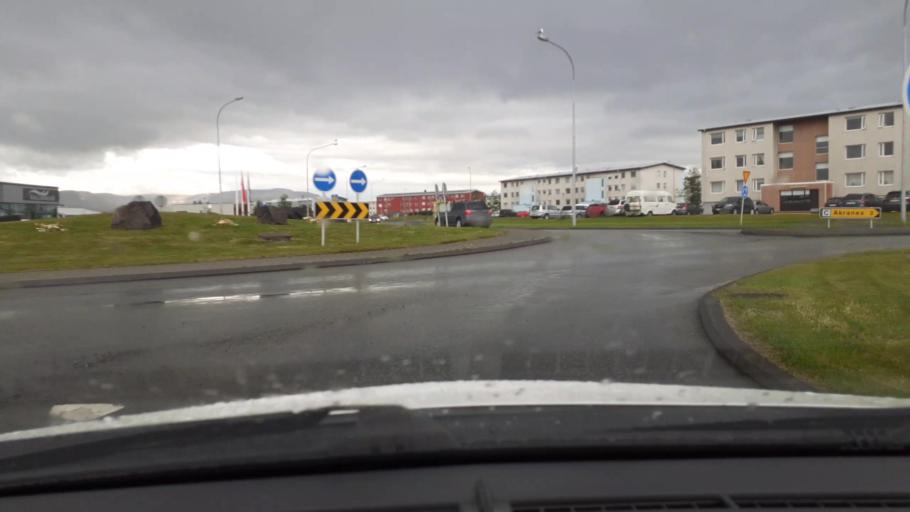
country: IS
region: West
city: Akranes
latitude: 64.3227
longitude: -22.0629
